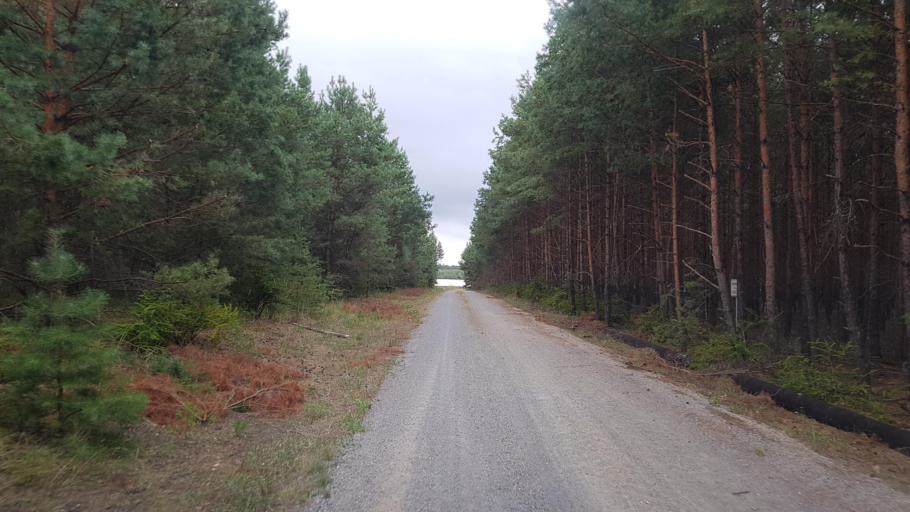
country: DE
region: Brandenburg
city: Finsterwalde
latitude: 51.5682
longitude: 13.7247
